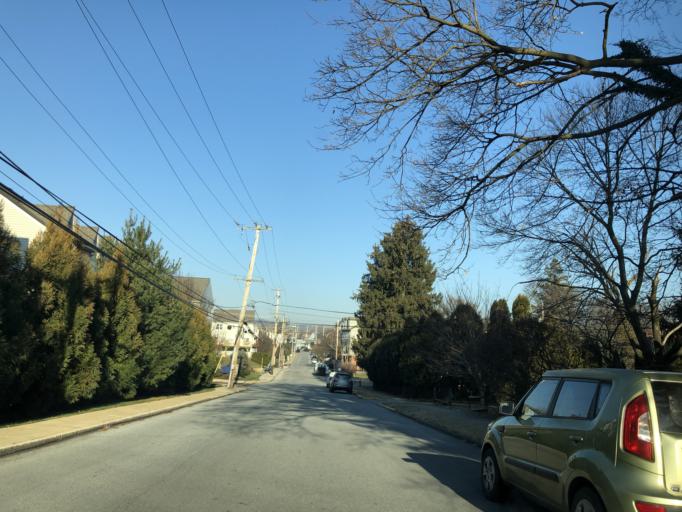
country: US
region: Pennsylvania
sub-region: Chester County
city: Downingtown
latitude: 40.0044
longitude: -75.6975
